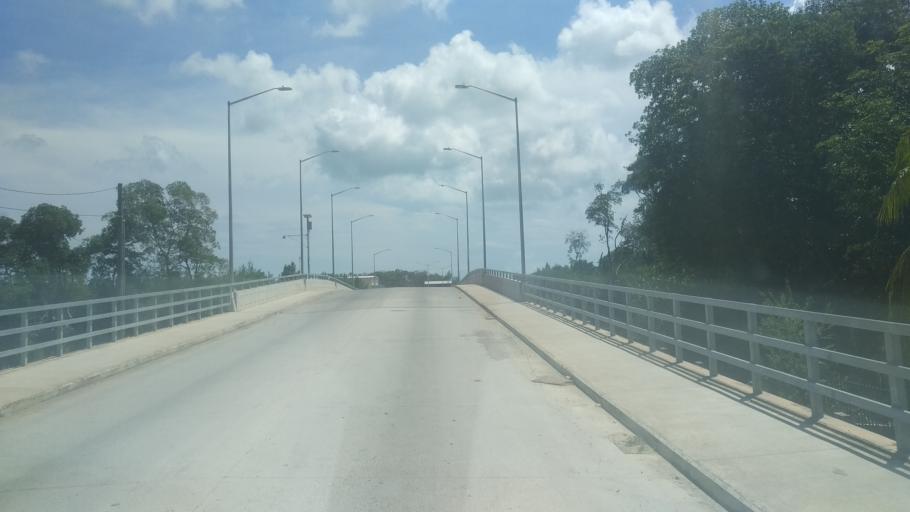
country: BZ
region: Belize
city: Belize City
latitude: 17.5084
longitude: -88.2215
